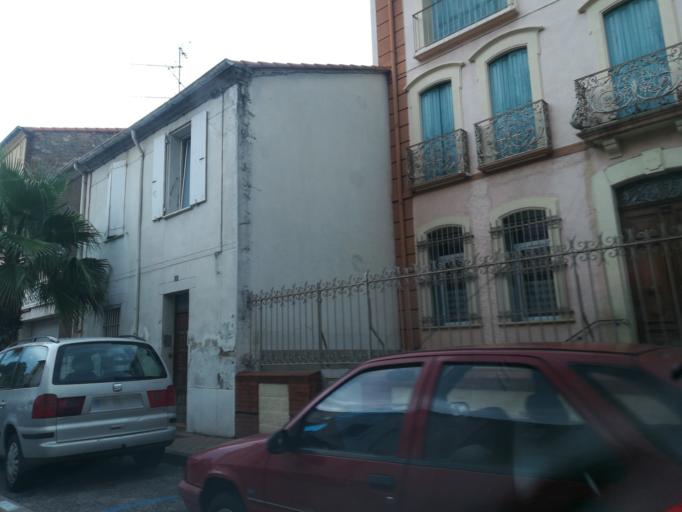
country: FR
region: Languedoc-Roussillon
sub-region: Departement des Pyrenees-Orientales
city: el Volo
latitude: 42.5239
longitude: 2.8317
